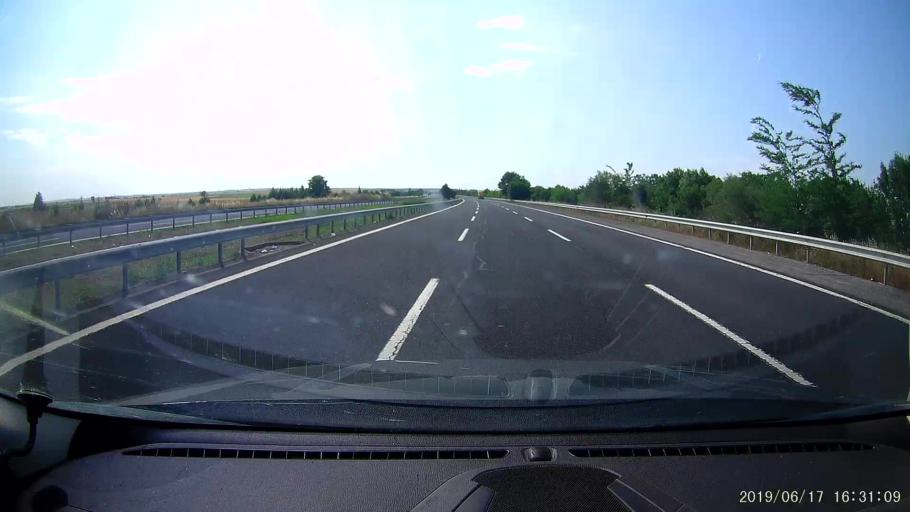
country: TR
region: Tekirdag
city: Beyazkoy
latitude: 41.3587
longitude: 27.6365
